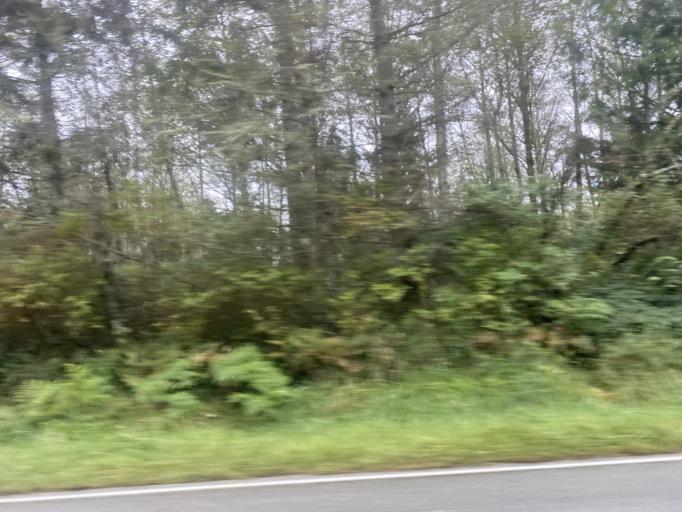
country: US
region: Washington
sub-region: Island County
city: Freeland
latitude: 48.0857
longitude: -122.4973
